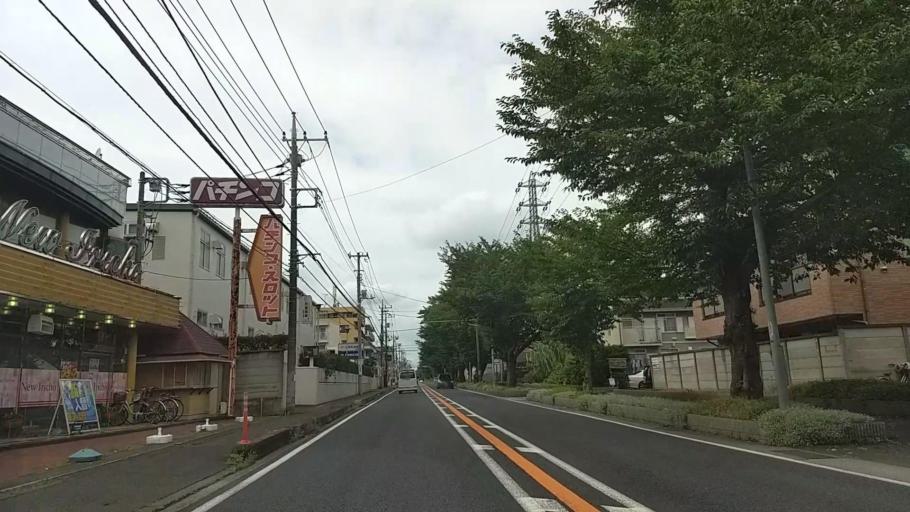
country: JP
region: Kanagawa
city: Minami-rinkan
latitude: 35.4420
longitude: 139.4671
